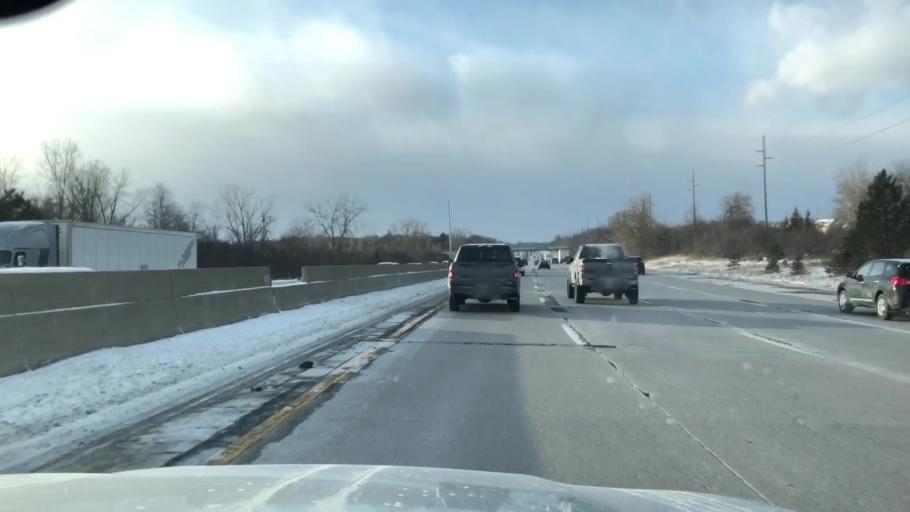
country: US
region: Michigan
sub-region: Oakland County
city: Franklin
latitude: 42.4921
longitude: -83.3330
